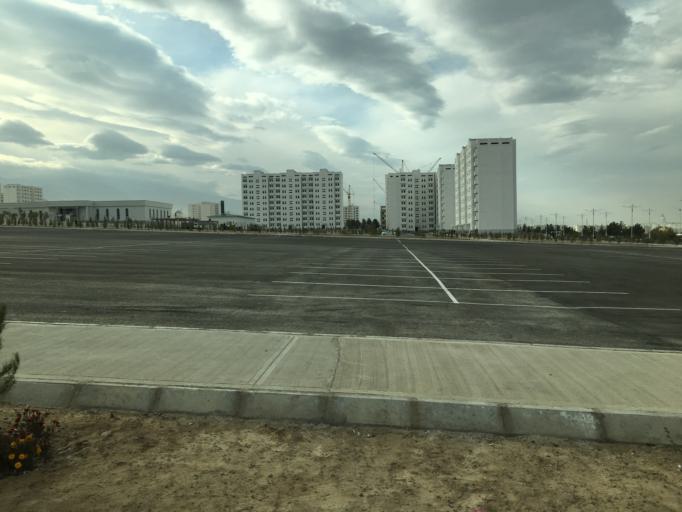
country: TM
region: Ahal
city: Ashgabat
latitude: 37.8996
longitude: 58.4151
